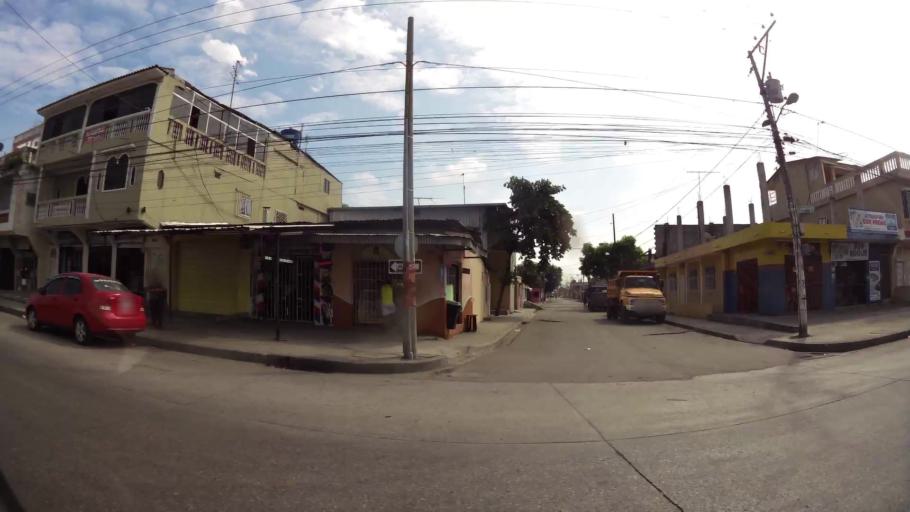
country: EC
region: Guayas
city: Guayaquil
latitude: -2.2590
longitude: -79.8873
